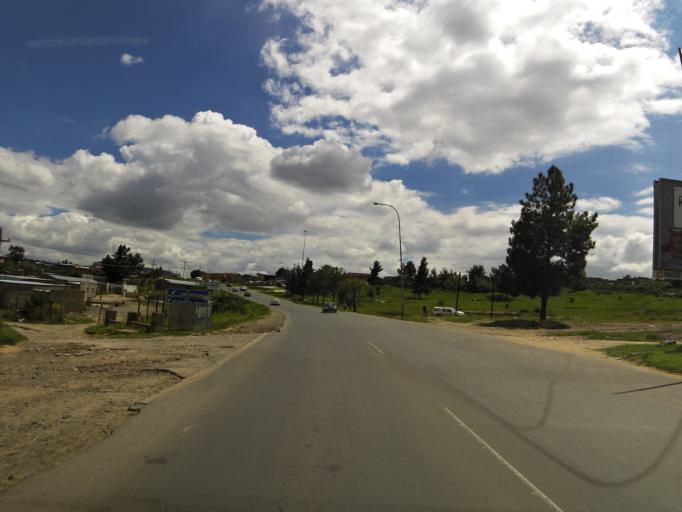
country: LS
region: Maseru
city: Maseru
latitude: -29.2987
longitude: 27.5177
